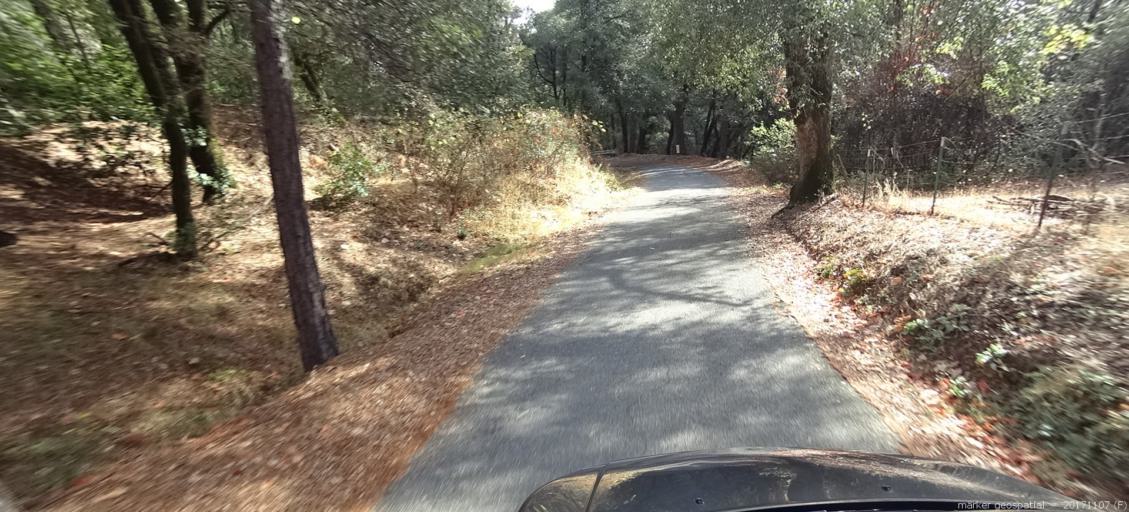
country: US
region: California
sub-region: Shasta County
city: Shasta
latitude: 40.5450
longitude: -122.5791
